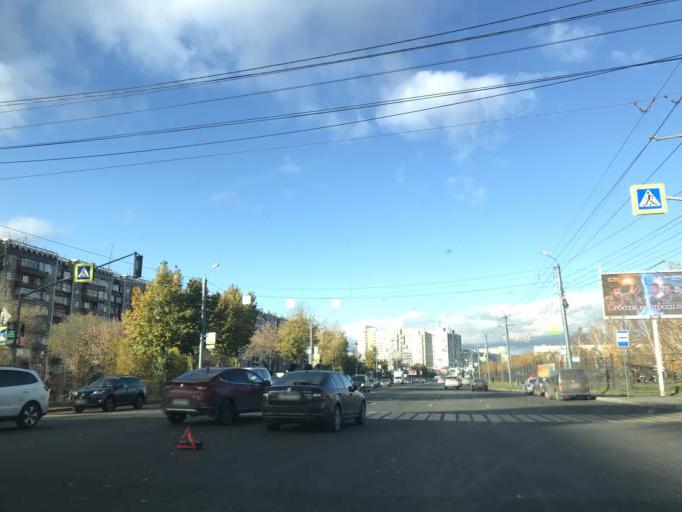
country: RU
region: Chelyabinsk
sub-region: Gorod Chelyabinsk
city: Chelyabinsk
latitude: 55.1670
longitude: 61.4527
